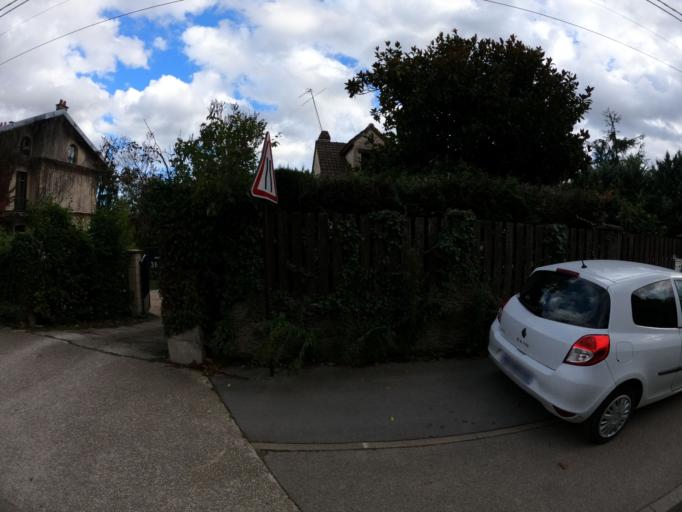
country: FR
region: Ile-de-France
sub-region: Departement de Seine-et-Marne
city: Esbly
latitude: 48.9060
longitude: 2.8140
